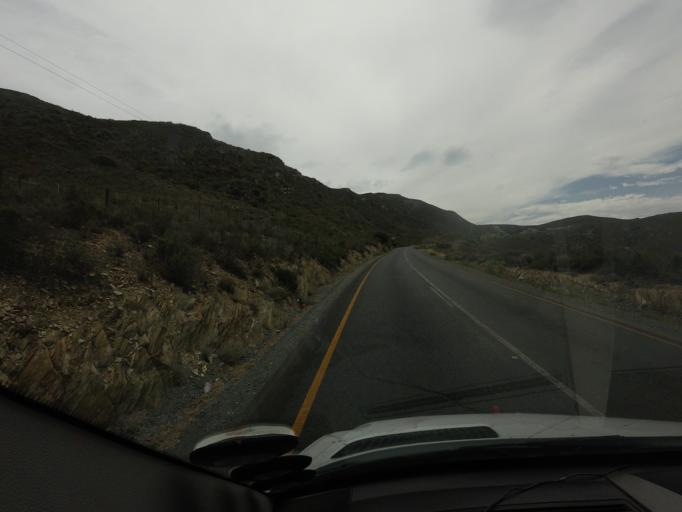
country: ZA
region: Western Cape
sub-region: Overberg District Municipality
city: Swellendam
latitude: -33.8968
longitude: 20.7237
